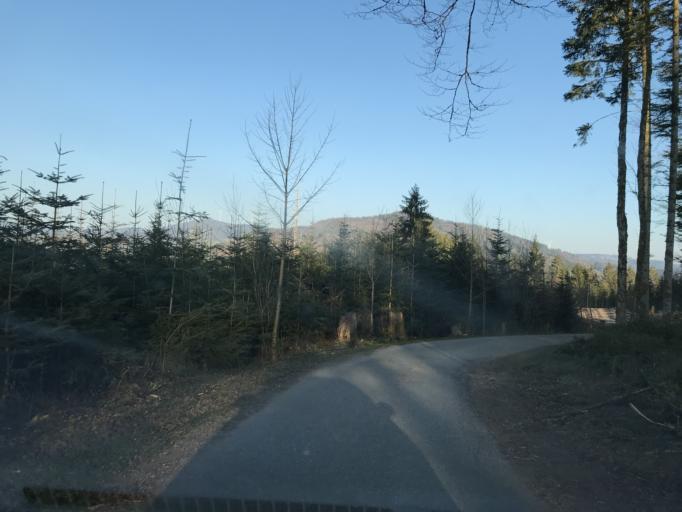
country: DE
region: Baden-Wuerttemberg
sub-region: Freiburg Region
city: Hausen
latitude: 47.6953
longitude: 7.8289
